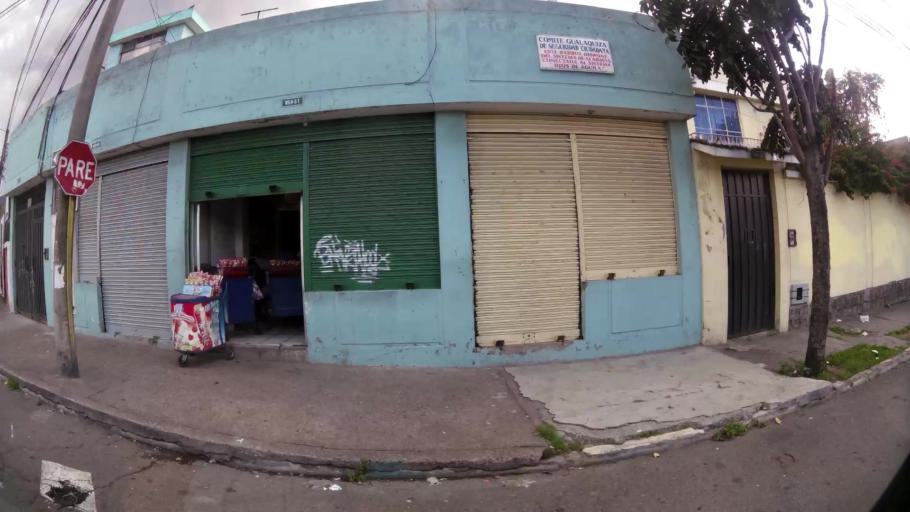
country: EC
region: Pichincha
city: Quito
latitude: -0.1265
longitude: -78.4918
